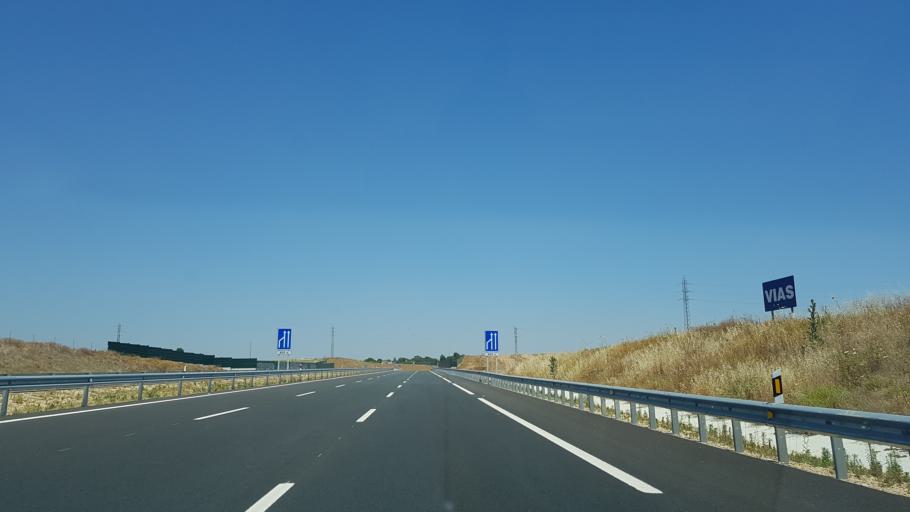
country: ES
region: Andalusia
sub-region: Provincia de Sevilla
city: Coria del Rio
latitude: 37.2992
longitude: -6.0672
